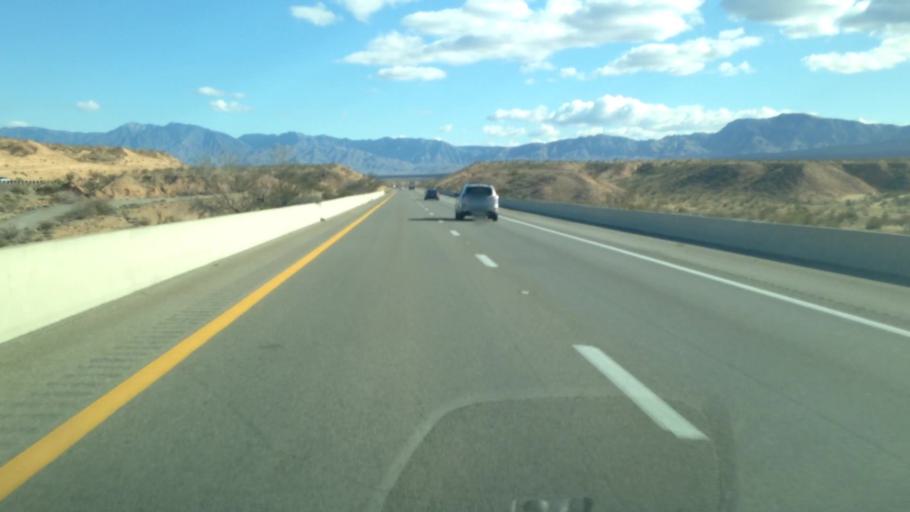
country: US
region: Nevada
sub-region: Clark County
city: Bunkerville
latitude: 36.7638
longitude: -114.1861
